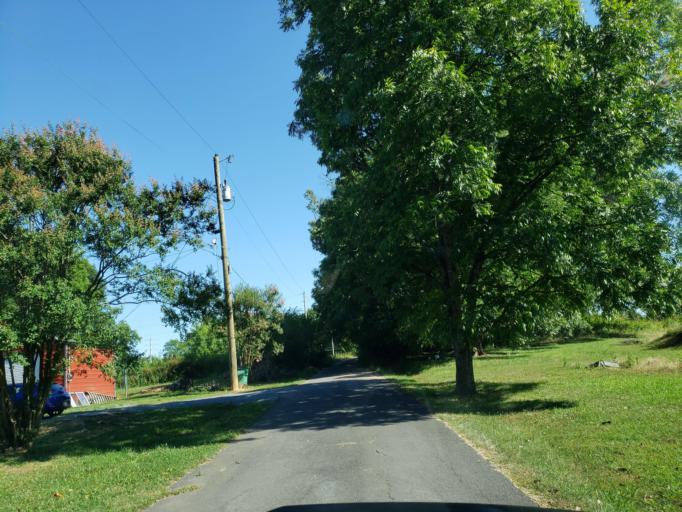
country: US
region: Georgia
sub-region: Gordon County
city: Calhoun
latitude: 34.5797
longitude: -84.9445
